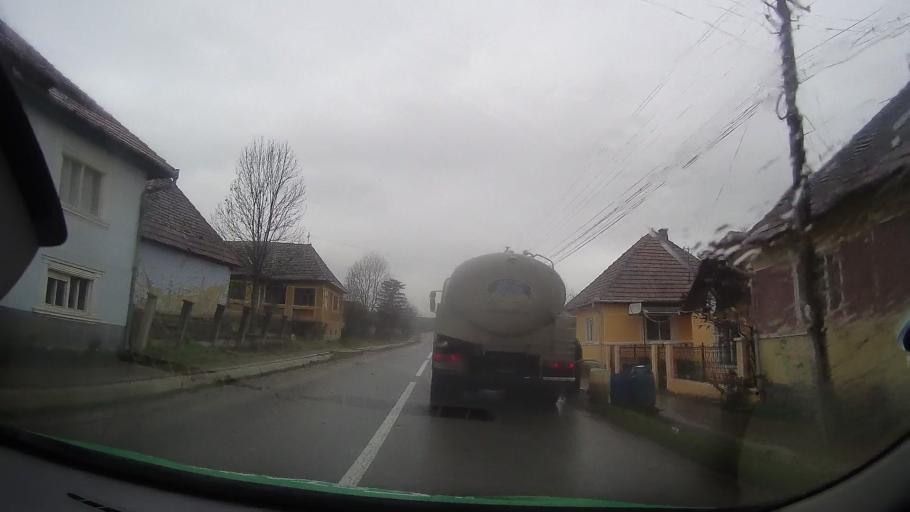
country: RO
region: Bistrita-Nasaud
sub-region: Comuna Monor
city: Monor
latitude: 46.9516
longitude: 24.6847
